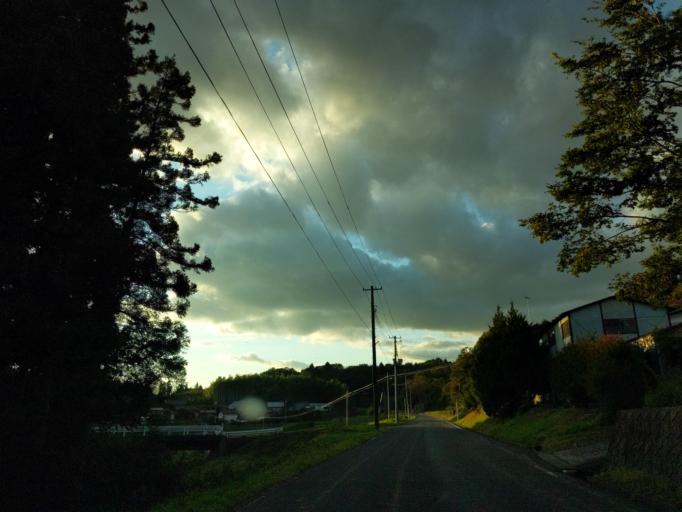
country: JP
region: Fukushima
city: Motomiya
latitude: 37.4758
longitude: 140.4347
